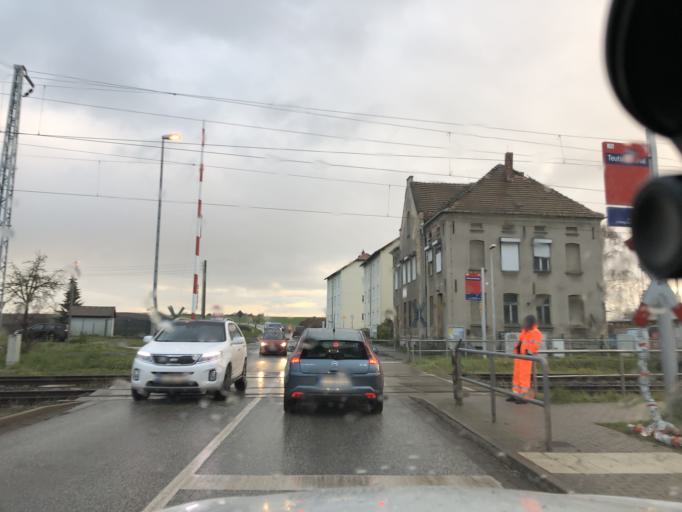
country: DE
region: Saxony-Anhalt
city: Langenbogen
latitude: 51.4647
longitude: 11.7837
